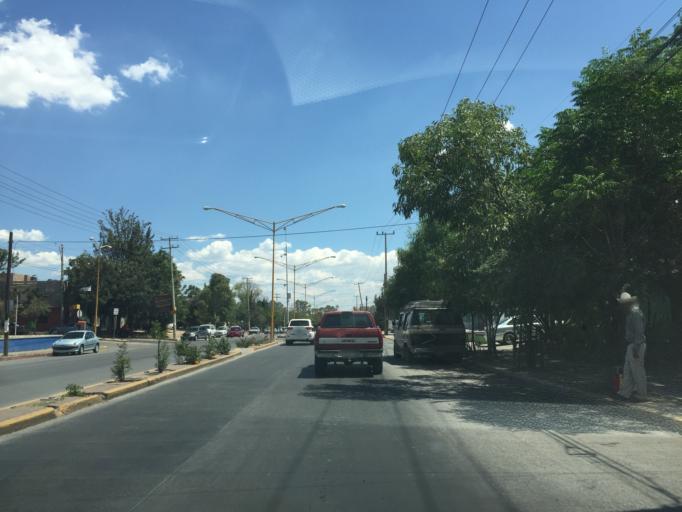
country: MX
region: Aguascalientes
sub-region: Aguascalientes
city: La Loma de los Negritos
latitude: 21.8496
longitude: -102.3191
